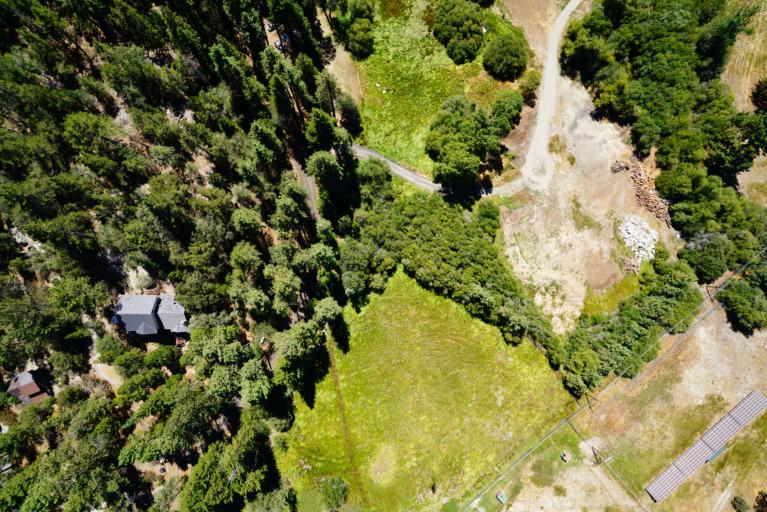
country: US
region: California
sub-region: Riverside County
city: Idyllwild-Pine Cove
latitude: 33.7545
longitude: -116.7285
